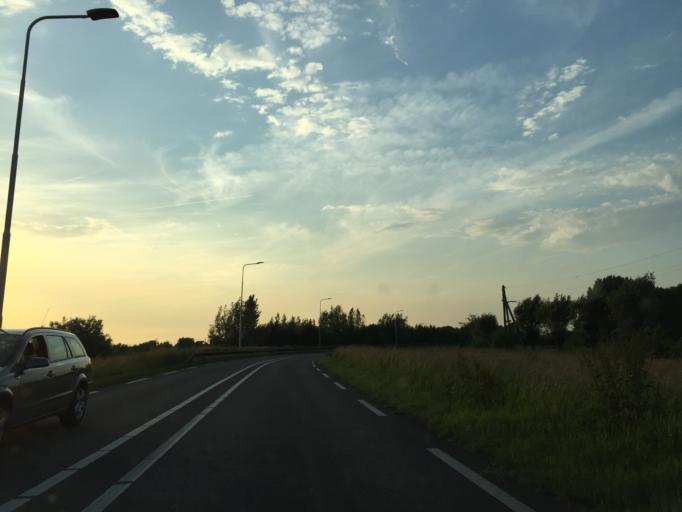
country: NL
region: South Holland
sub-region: Gemeente Vlist
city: Haastrecht
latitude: 51.9869
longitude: 4.7509
